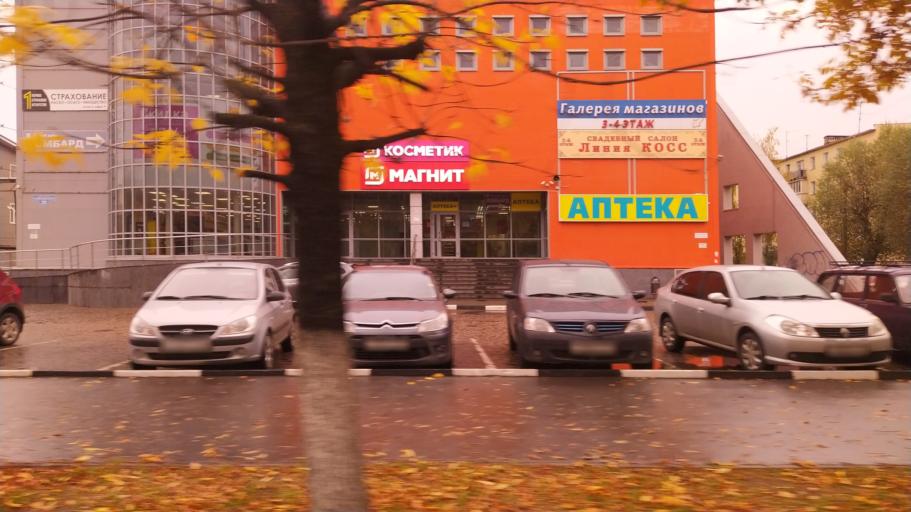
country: RU
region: Tverskaya
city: Tver
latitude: 56.8421
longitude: 35.8996
